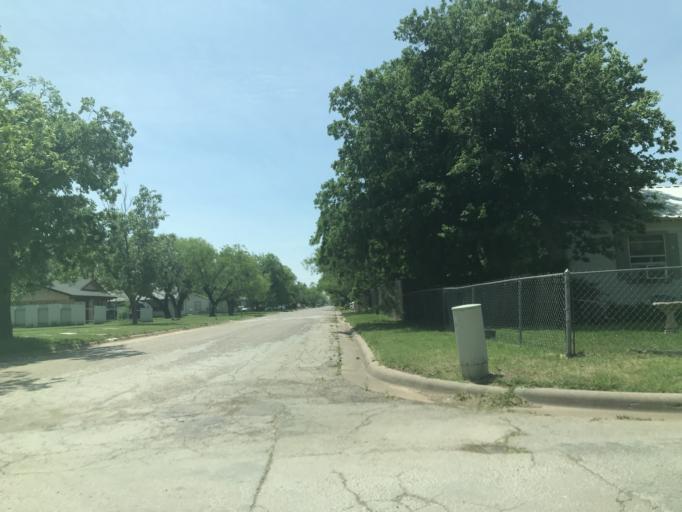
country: US
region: Texas
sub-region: Taylor County
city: Abilene
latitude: 32.4475
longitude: -99.7616
